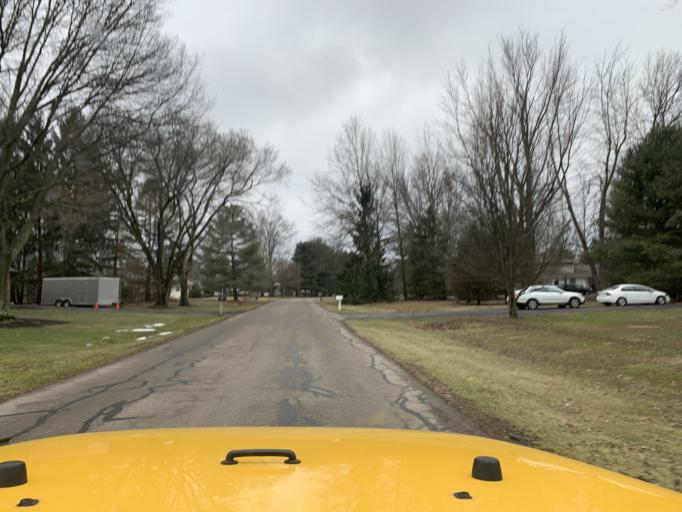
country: US
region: Ohio
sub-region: Franklin County
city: New Albany
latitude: 40.0965
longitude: -82.8028
